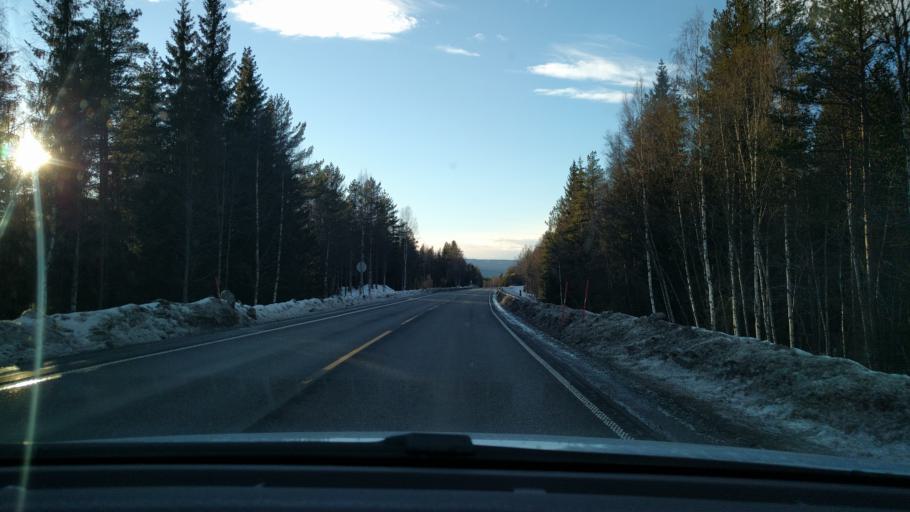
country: NO
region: Hedmark
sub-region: Elverum
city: Elverum
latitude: 61.0105
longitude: 11.8166
